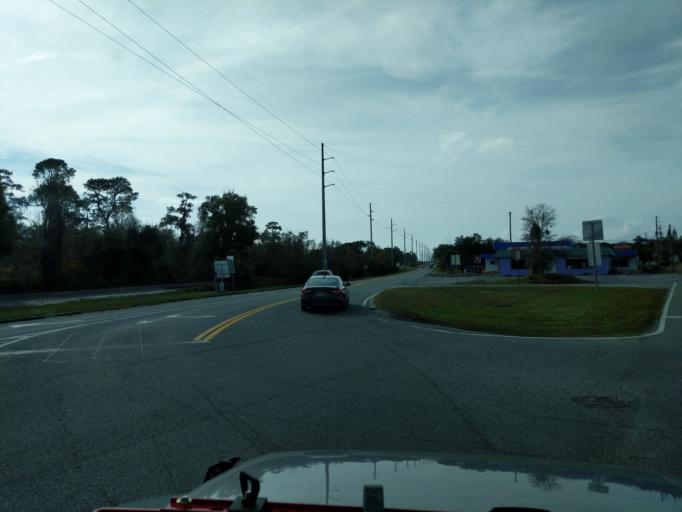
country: US
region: Florida
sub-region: Lake County
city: Mount Dora
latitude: 28.8077
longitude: -81.6749
